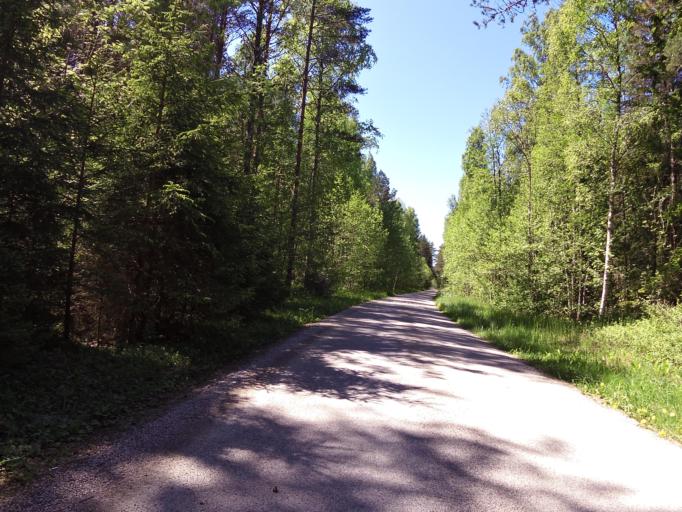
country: EE
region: Harju
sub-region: Paldiski linn
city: Paldiski
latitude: 59.2689
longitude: 23.7738
